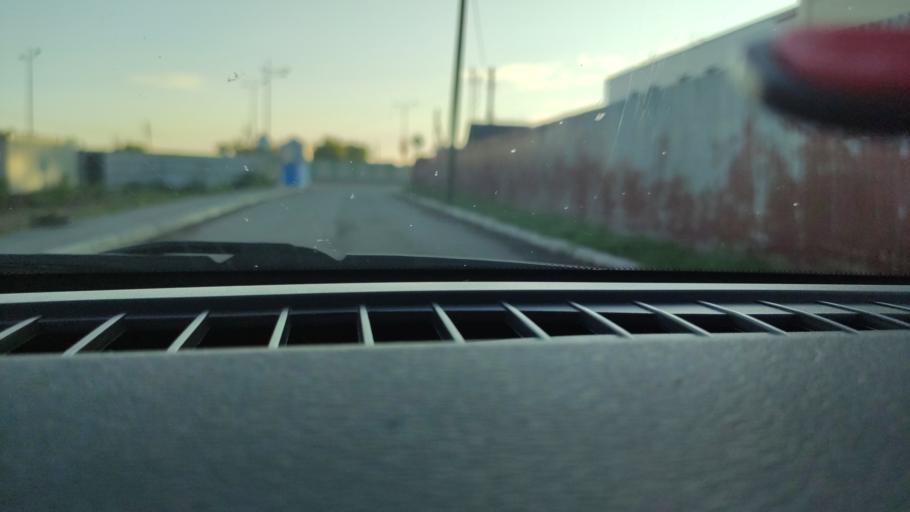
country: RU
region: Perm
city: Kondratovo
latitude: 57.9369
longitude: 56.0434
